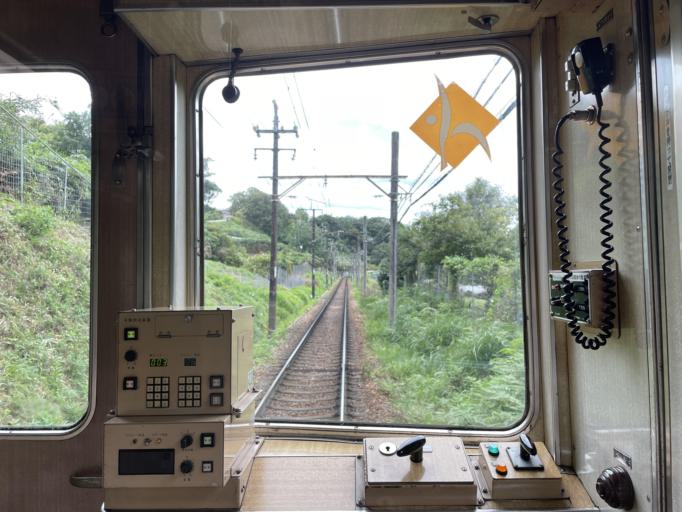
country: JP
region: Osaka
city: Ikeda
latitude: 34.8946
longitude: 135.4220
